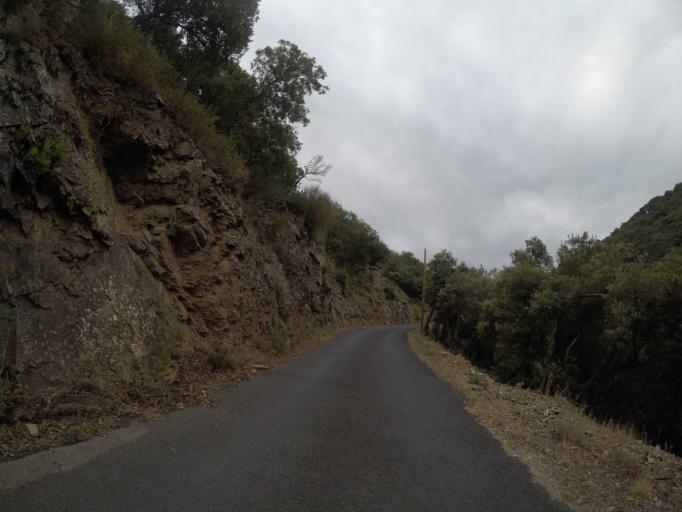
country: FR
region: Languedoc-Roussillon
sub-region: Departement des Pyrenees-Orientales
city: Ille-sur-Tet
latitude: 42.6390
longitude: 2.6205
